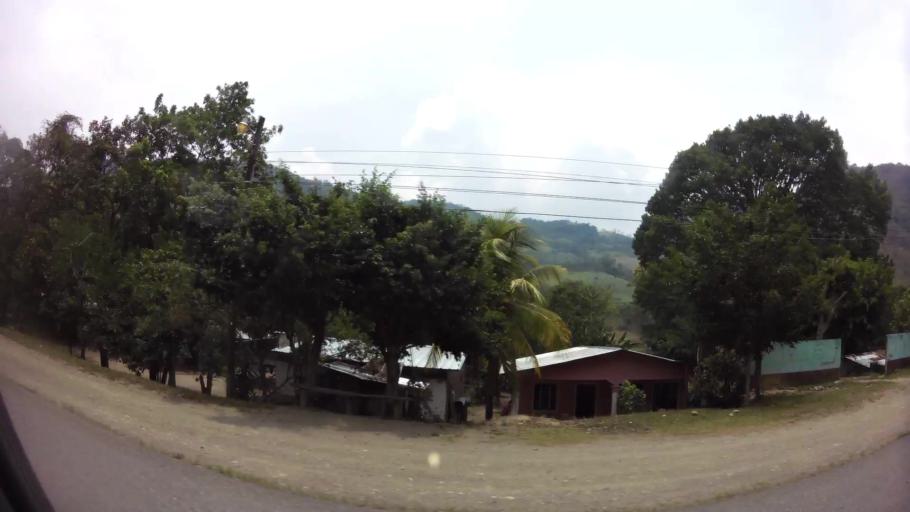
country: HN
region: Comayagua
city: Taulabe
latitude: 14.7324
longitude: -87.9640
